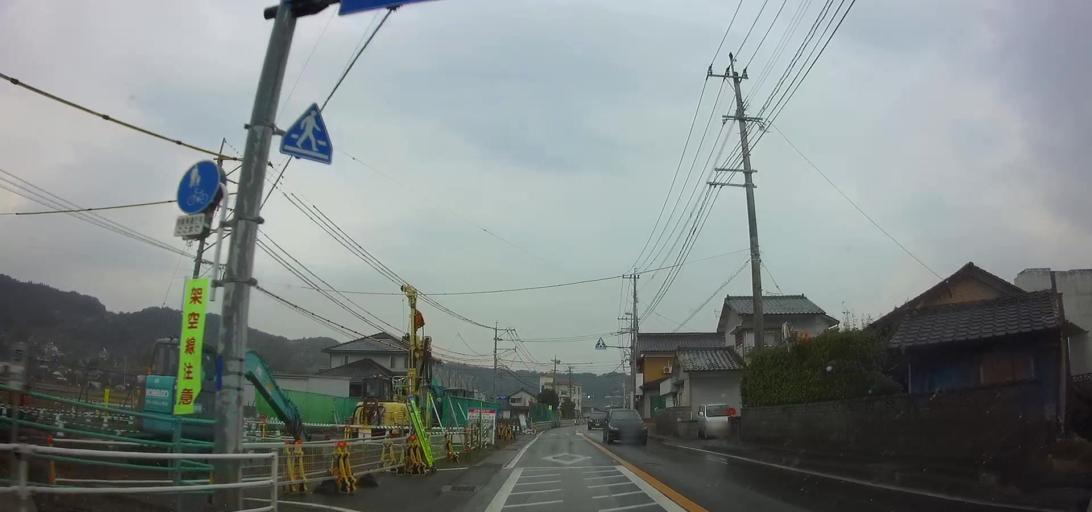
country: JP
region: Nagasaki
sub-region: Isahaya-shi
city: Isahaya
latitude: 32.8345
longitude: 130.1136
